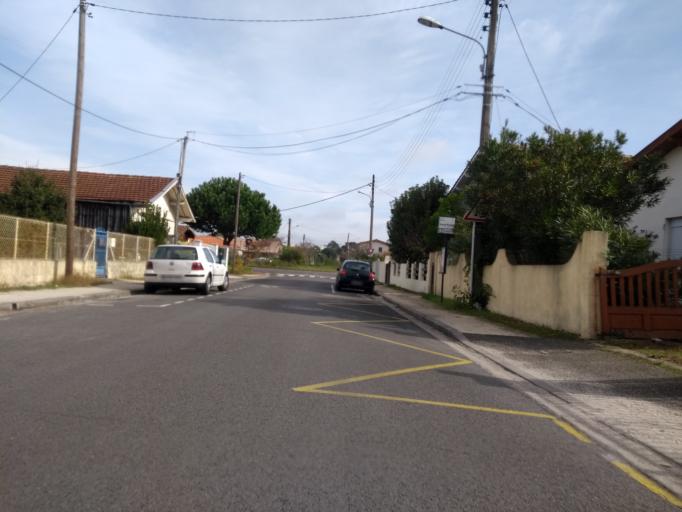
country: FR
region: Aquitaine
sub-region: Departement de la Gironde
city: Talence
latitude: 44.8052
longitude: -0.6169
